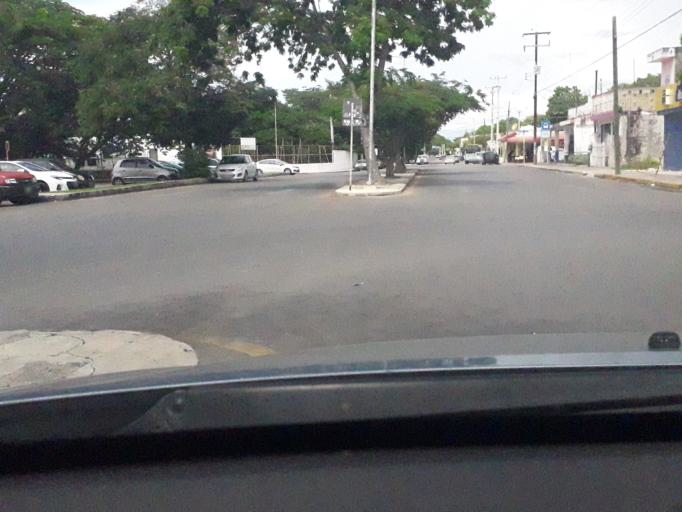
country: MX
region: Yucatan
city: Merida
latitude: 20.9728
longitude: -89.6561
